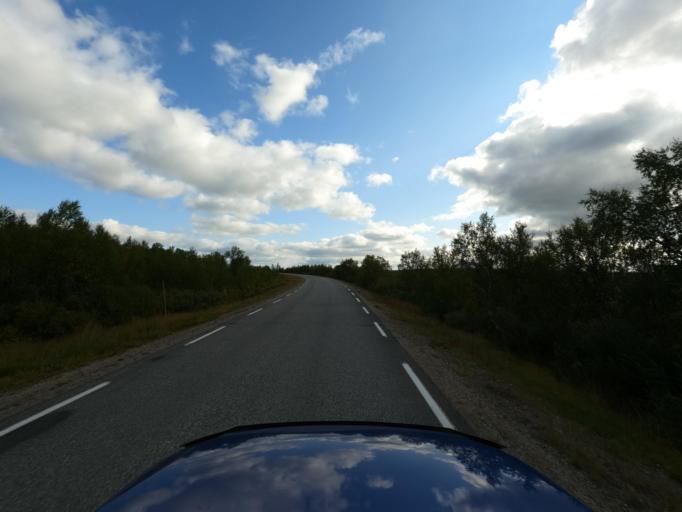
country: NO
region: Finnmark Fylke
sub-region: Porsanger
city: Lakselv
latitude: 69.3736
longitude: 24.4148
